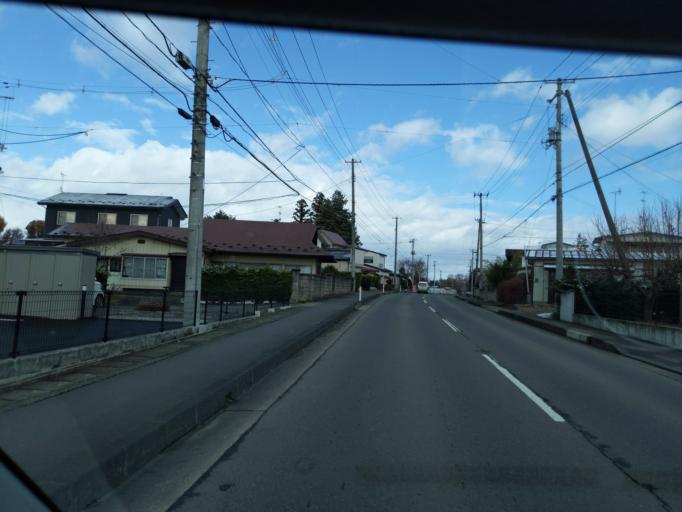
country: JP
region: Iwate
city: Mizusawa
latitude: 39.1166
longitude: 141.1378
